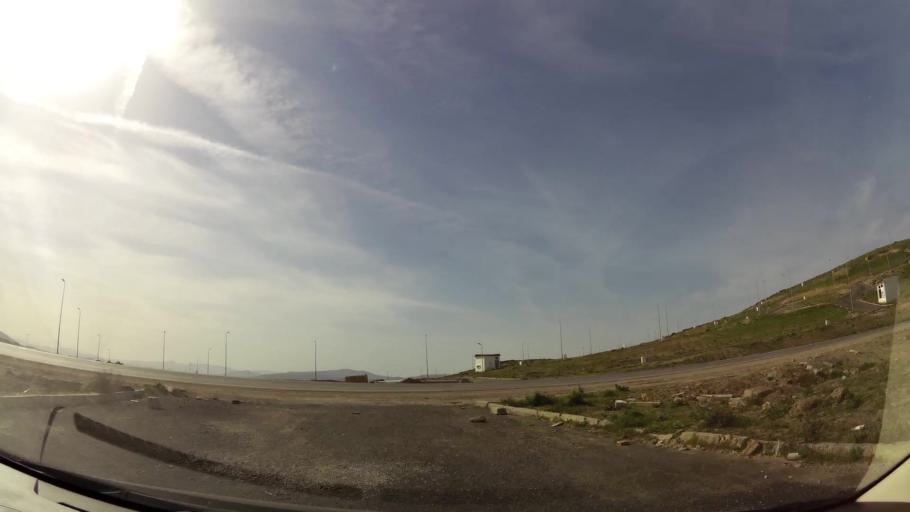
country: MA
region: Tanger-Tetouan
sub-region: Tanger-Assilah
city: Tangier
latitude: 35.7014
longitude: -5.8170
